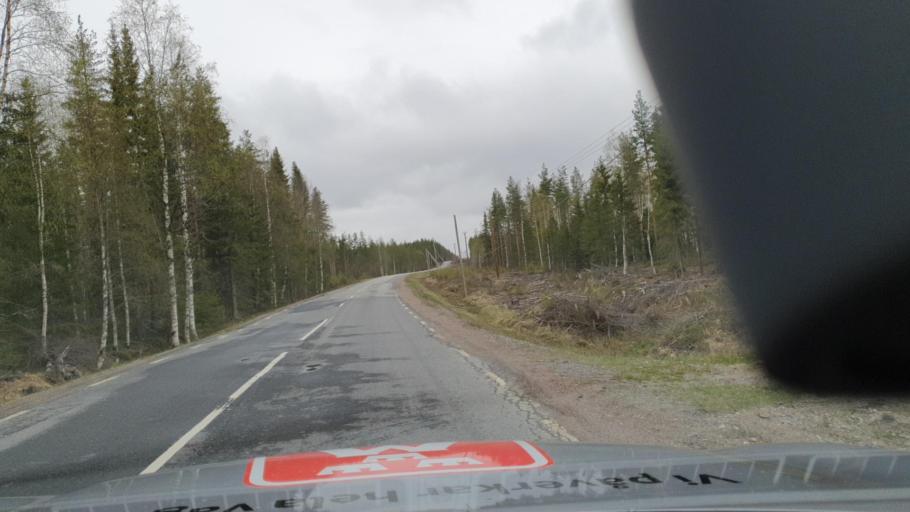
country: SE
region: Vaesternorrland
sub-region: Solleftea Kommun
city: Solleftea
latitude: 63.5950
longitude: 17.5519
